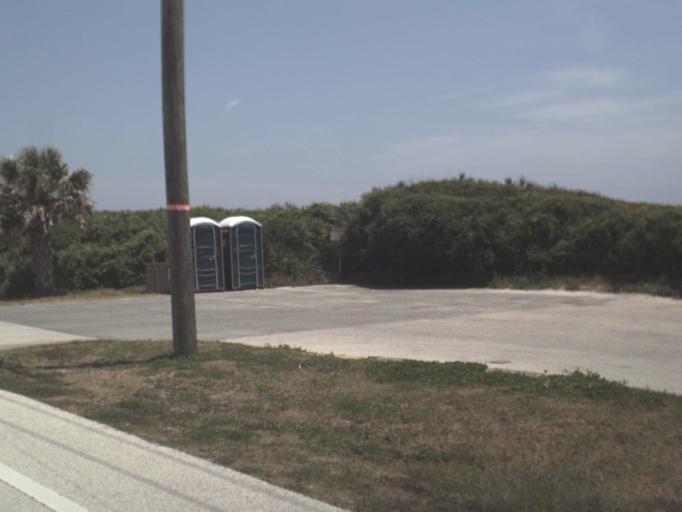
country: US
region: Florida
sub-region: Saint Johns County
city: Villano Beach
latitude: 29.9907
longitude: -81.3153
